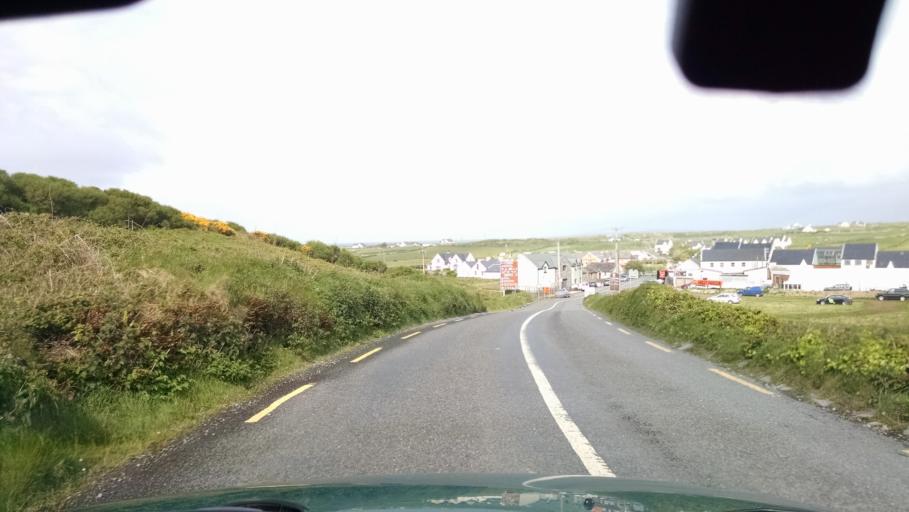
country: IE
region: Connaught
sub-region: County Galway
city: Bearna
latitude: 53.0151
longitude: -9.3746
